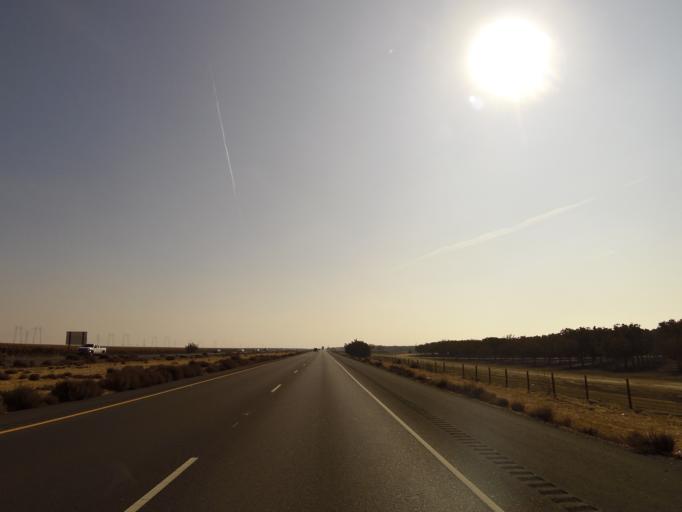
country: US
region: California
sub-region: Kings County
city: Kettleman City
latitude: 35.9210
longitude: -119.8985
